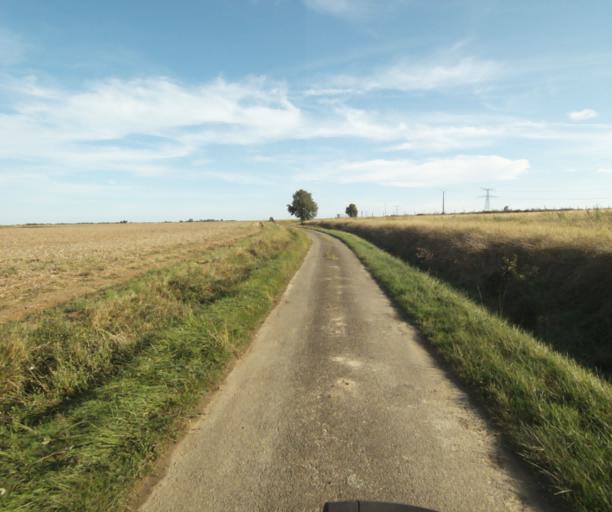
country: FR
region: Midi-Pyrenees
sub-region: Departement du Tarn-et-Garonne
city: Finhan
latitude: 43.9104
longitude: 1.1098
